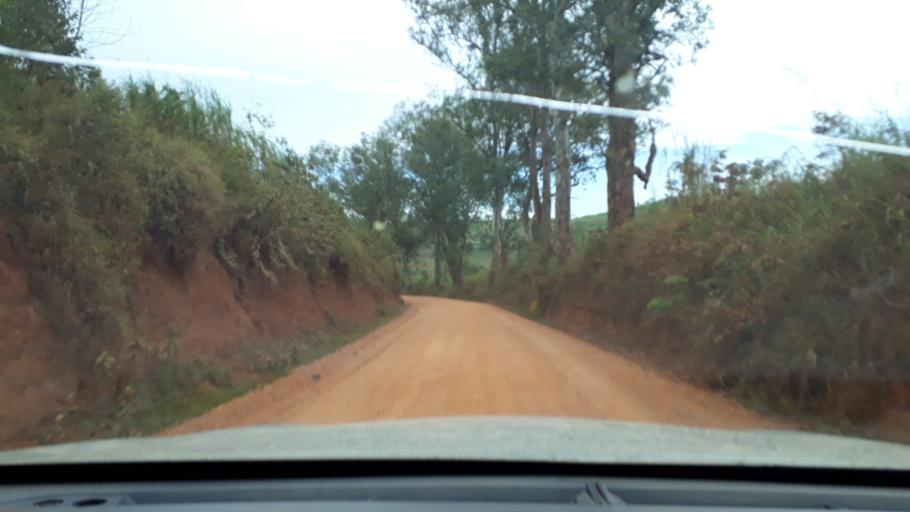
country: CD
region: Eastern Province
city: Bunia
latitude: 1.8325
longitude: 30.4551
